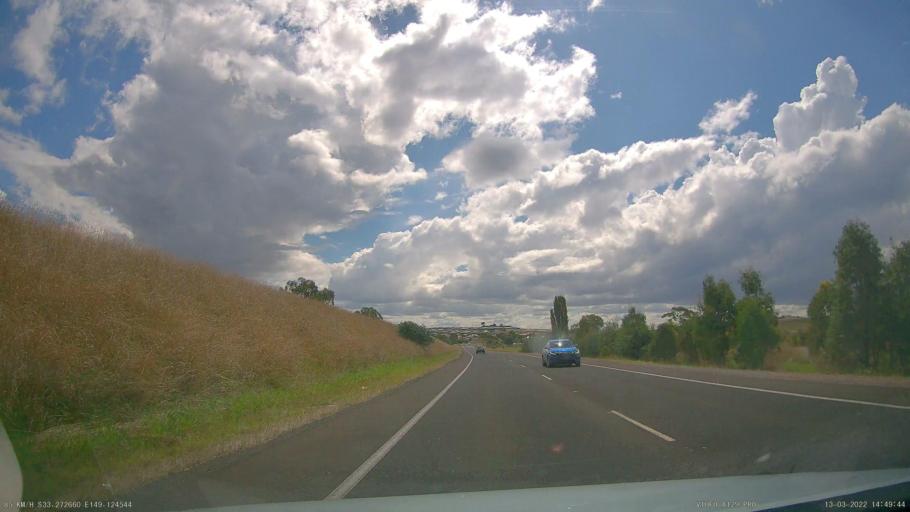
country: AU
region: New South Wales
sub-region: Orange Municipality
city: Orange
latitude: -33.2724
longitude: 149.1242
